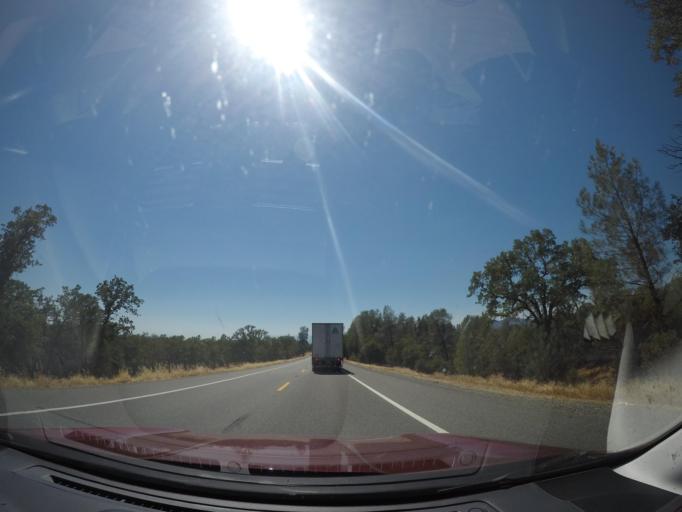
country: US
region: California
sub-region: Shasta County
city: Bella Vista
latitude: 40.6871
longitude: -122.1372
